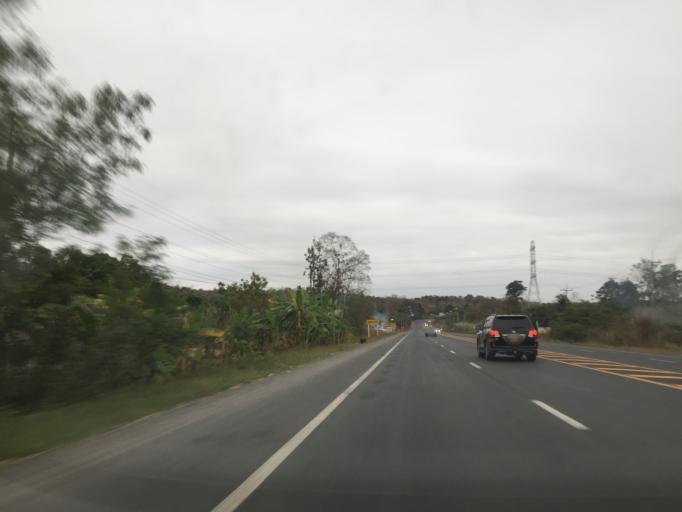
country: TH
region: Loei
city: Erawan
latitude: 17.3153
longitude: 101.9222
